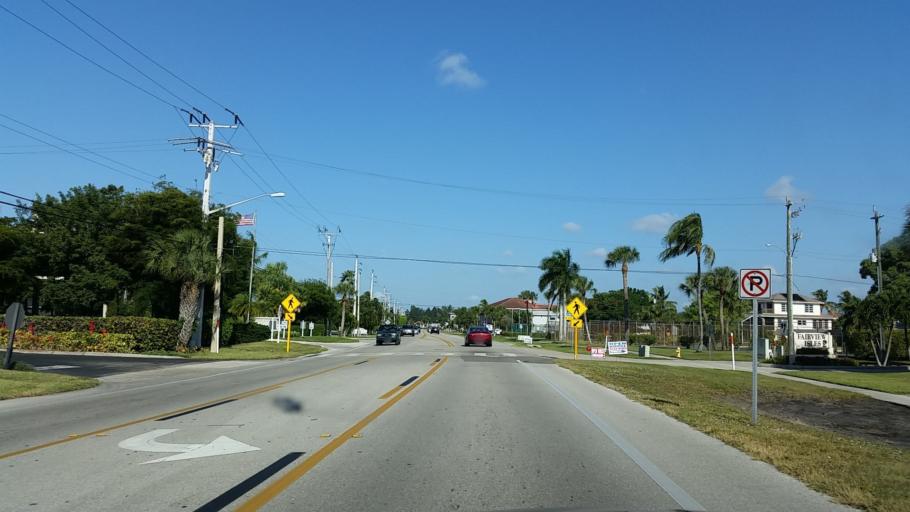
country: US
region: Florida
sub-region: Lee County
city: Fort Myers Beach
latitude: 26.4195
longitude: -81.9025
